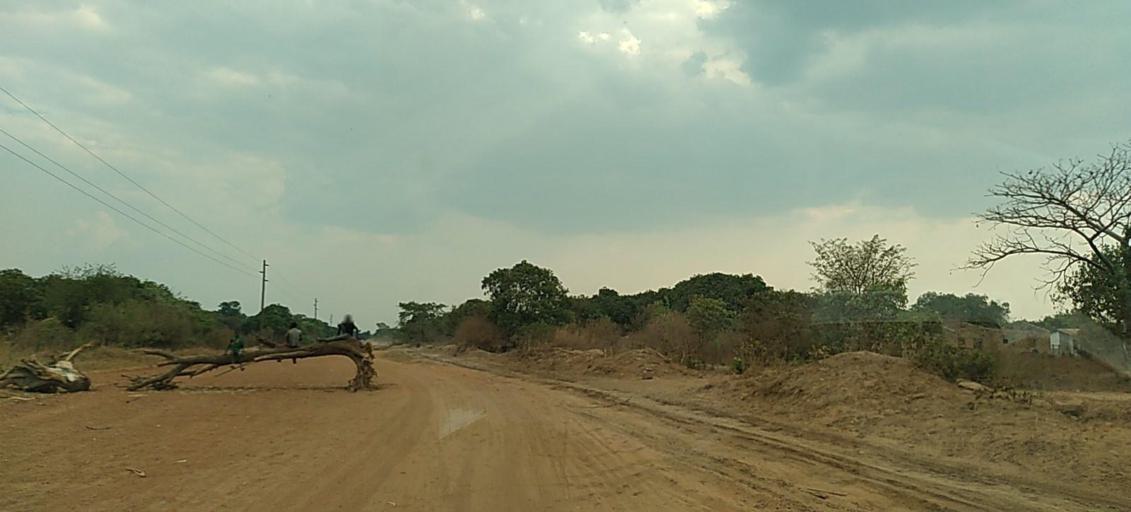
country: ZM
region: Copperbelt
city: Kalulushi
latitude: -12.8920
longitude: 27.9505
